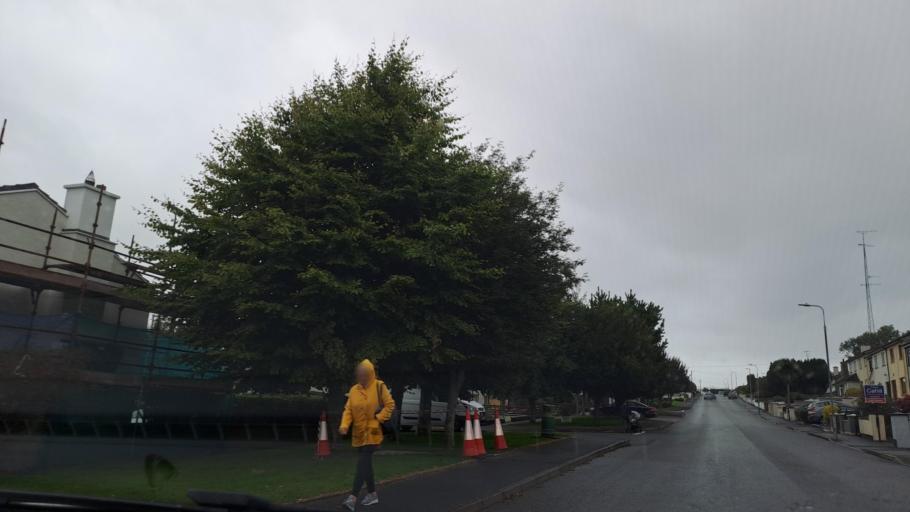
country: IE
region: Ulster
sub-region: County Monaghan
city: Carrickmacross
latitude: 53.9797
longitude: -6.7128
